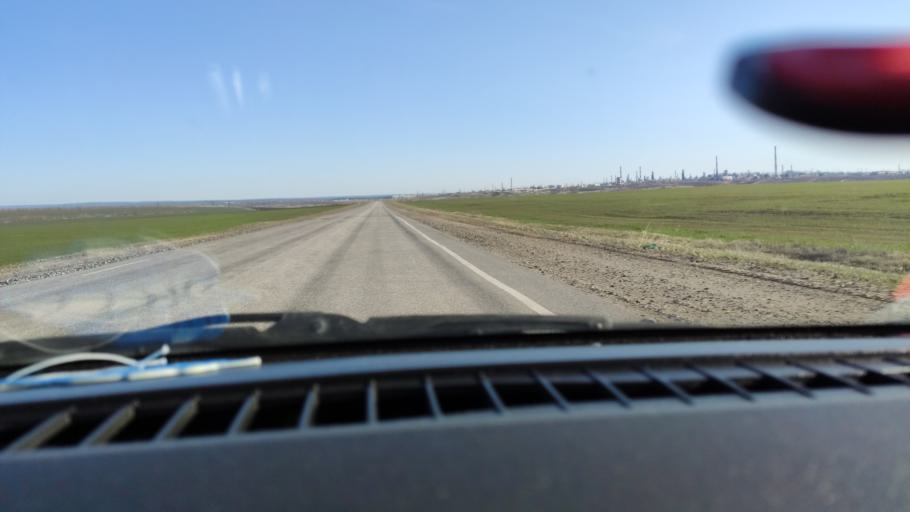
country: RU
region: Samara
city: Varlamovo
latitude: 53.0534
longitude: 48.3471
